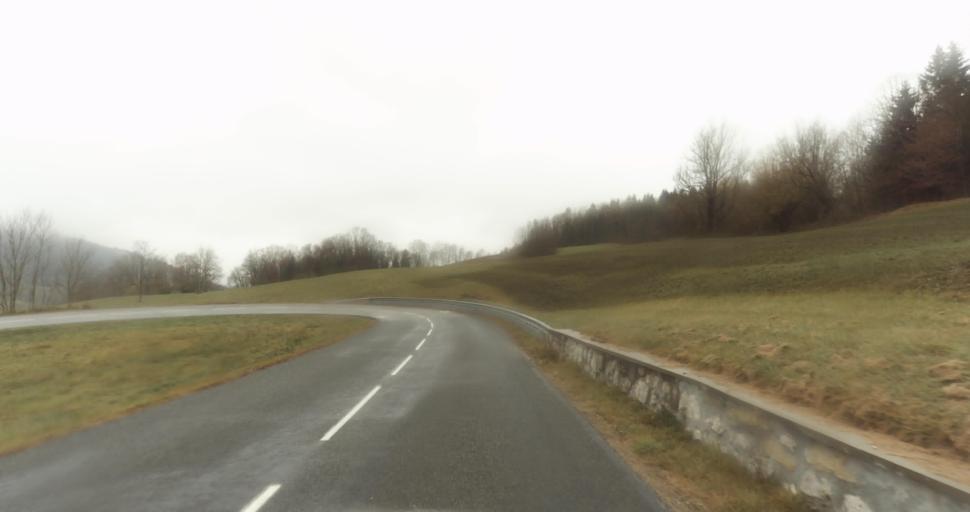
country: FR
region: Rhone-Alpes
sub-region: Departement de la Haute-Savoie
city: Thorens-Glieres
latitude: 46.0194
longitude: 6.2802
